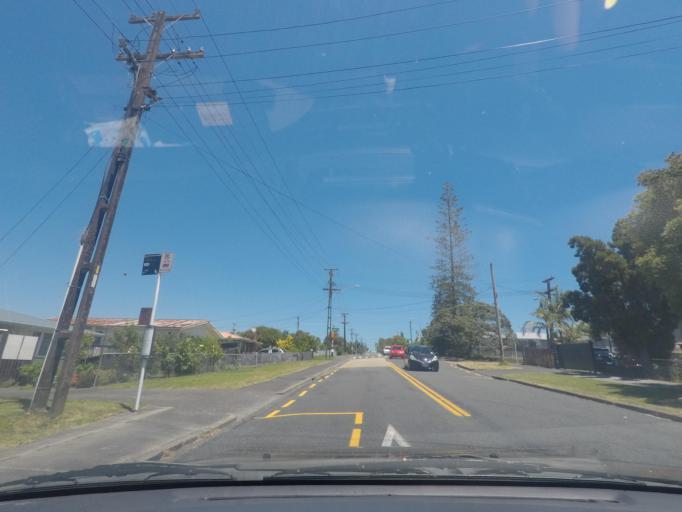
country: NZ
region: Auckland
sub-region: Auckland
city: Waitakere
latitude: -36.9150
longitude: 174.7158
